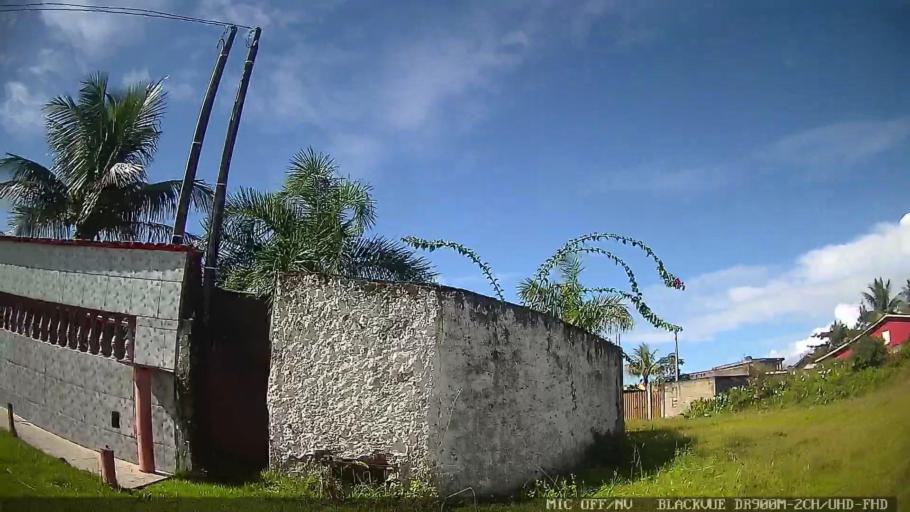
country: BR
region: Sao Paulo
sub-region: Itanhaem
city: Itanhaem
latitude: -24.2357
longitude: -46.8929
